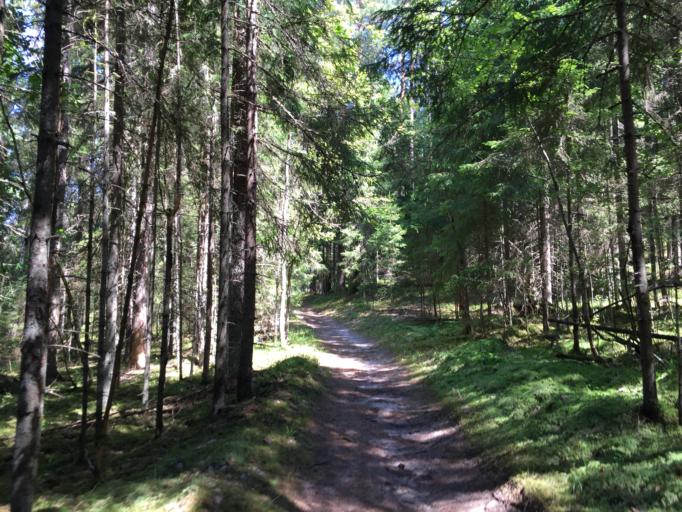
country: LV
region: Sigulda
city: Sigulda
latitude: 57.2247
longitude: 24.9122
